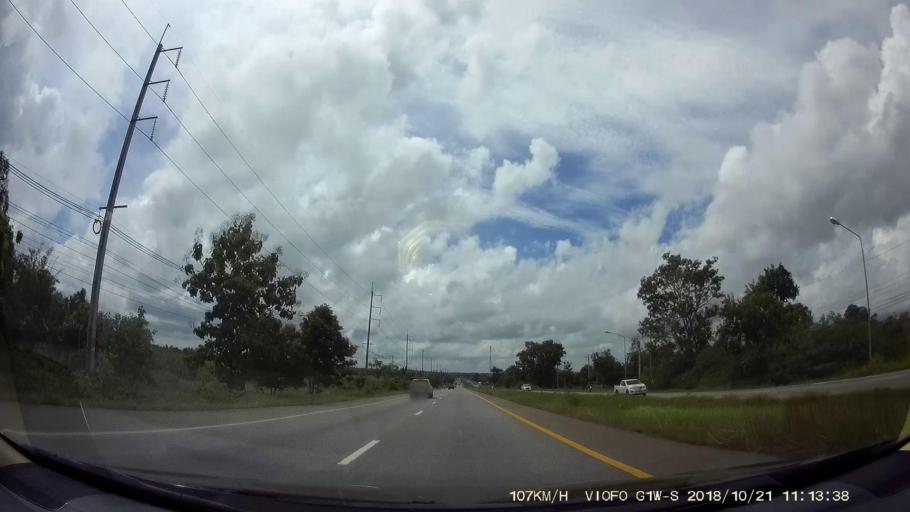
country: TH
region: Chaiyaphum
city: Chaiyaphum
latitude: 15.9140
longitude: 102.1310
